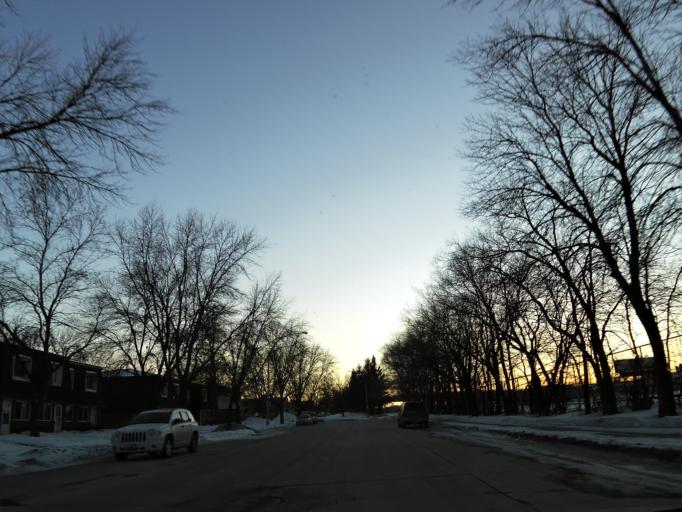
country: US
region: North Dakota
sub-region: Grand Forks County
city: Grand Forks
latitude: 47.9213
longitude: -97.0347
